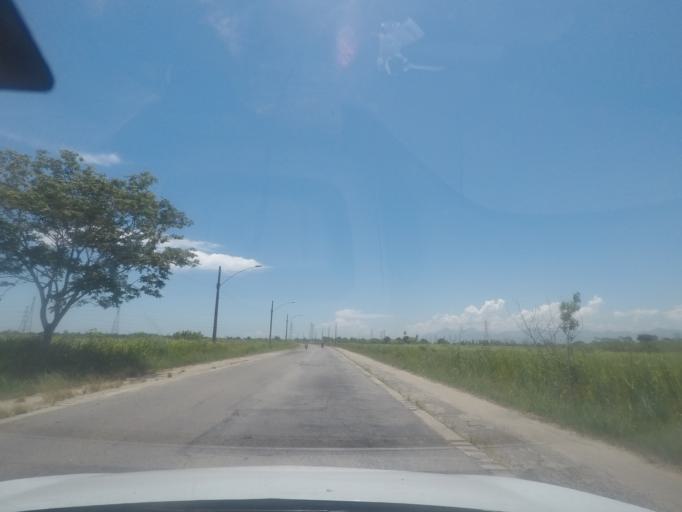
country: BR
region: Rio de Janeiro
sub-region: Itaguai
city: Itaguai
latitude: -22.8961
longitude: -43.6838
